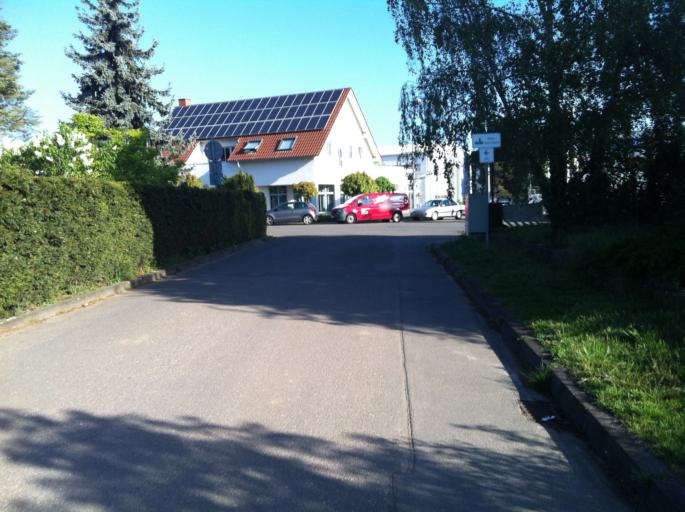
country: DE
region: Rheinland-Pfalz
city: Budenheim
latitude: 49.9958
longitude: 8.2122
